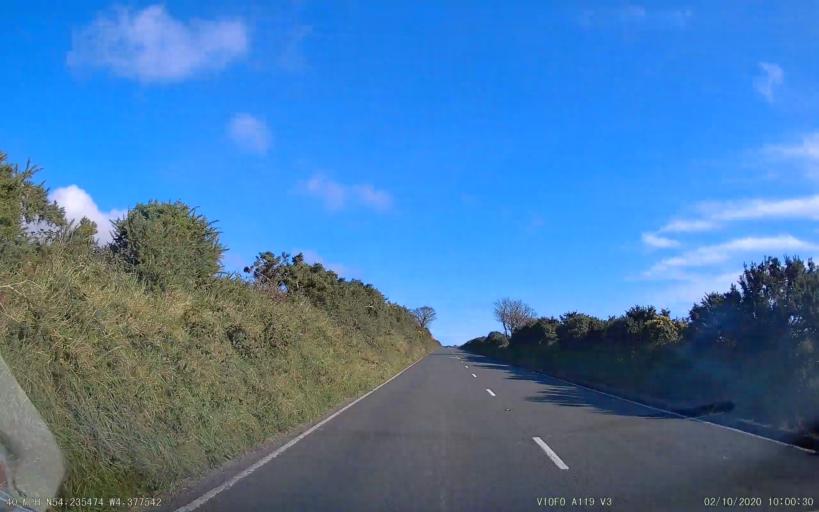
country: IM
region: Laxey
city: Laxey
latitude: 54.2355
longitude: -4.3775
